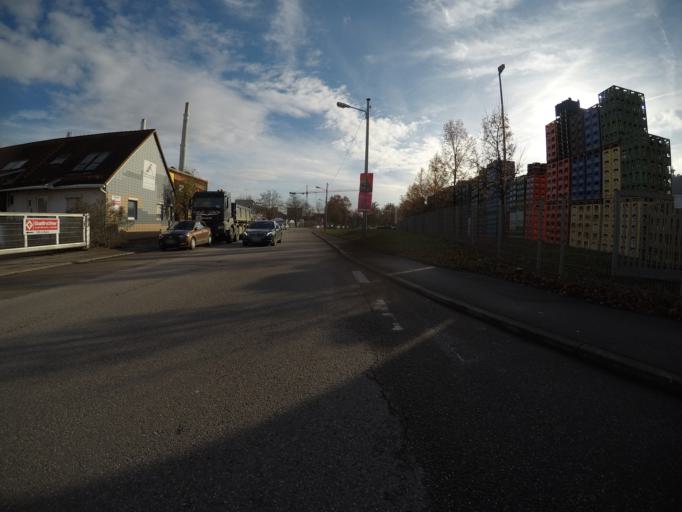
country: DE
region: Baden-Wuerttemberg
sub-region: Regierungsbezirk Stuttgart
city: Stuttgart-Ost
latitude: 48.7832
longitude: 9.2259
